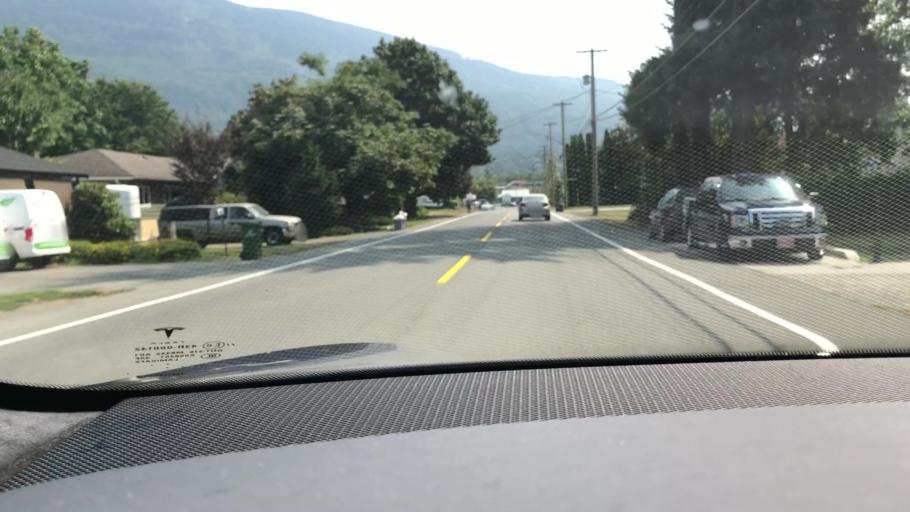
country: CA
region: British Columbia
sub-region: Fraser Valley Regional District
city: Chilliwack
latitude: 49.0842
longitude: -122.0649
